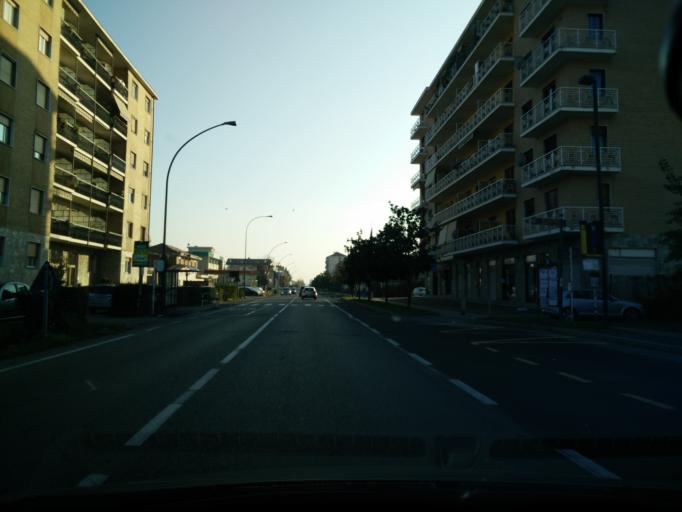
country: IT
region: Piedmont
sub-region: Provincia di Torino
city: Leini
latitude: 45.1683
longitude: 7.7124
